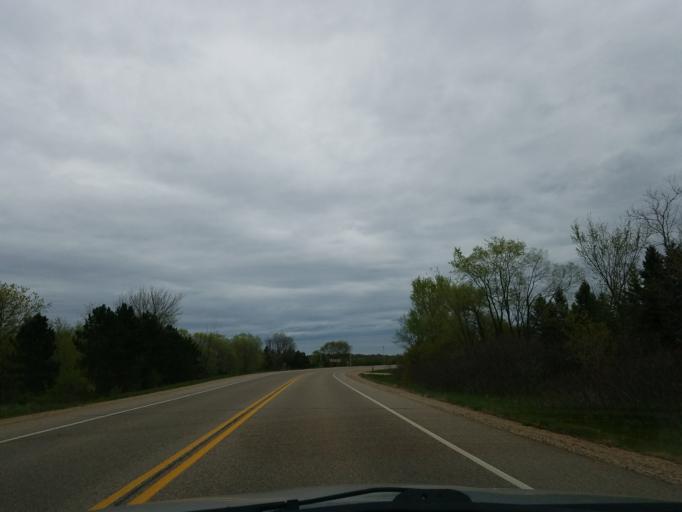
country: US
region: Minnesota
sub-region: Washington County
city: Bayport
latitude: 45.0297
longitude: -92.7496
